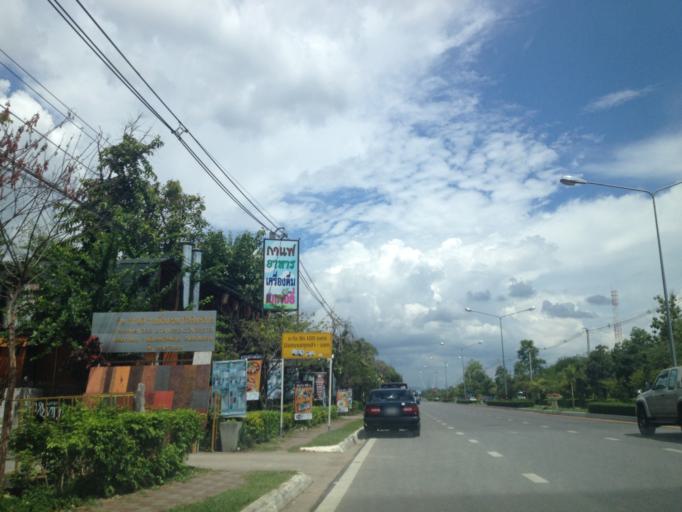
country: TH
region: Chiang Mai
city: Hang Dong
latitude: 18.7348
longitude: 98.9376
